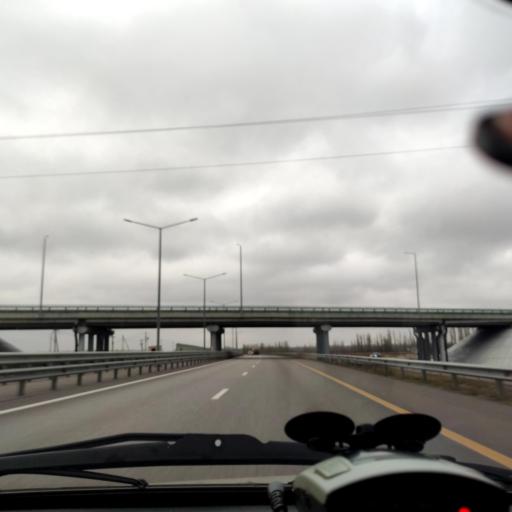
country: RU
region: Voronezj
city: Novaya Usman'
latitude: 51.5907
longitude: 39.3731
